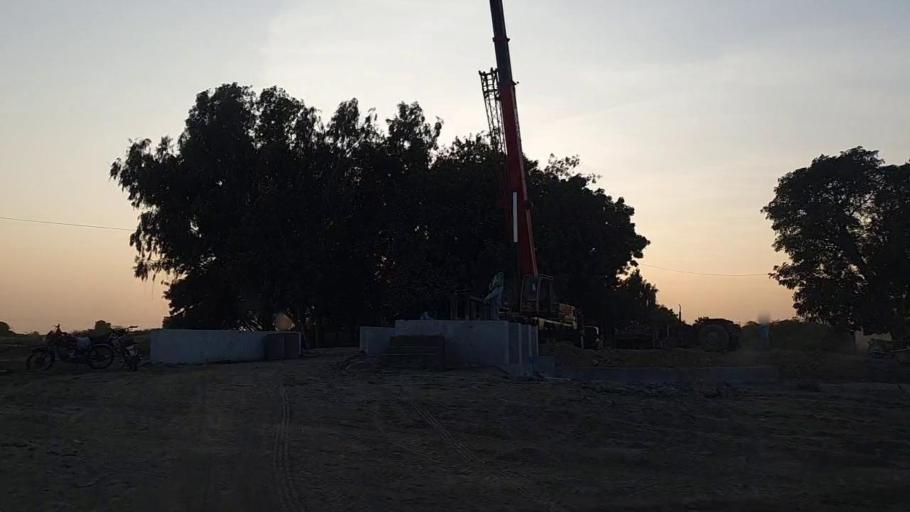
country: PK
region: Sindh
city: Naukot
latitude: 24.9499
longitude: 69.4302
